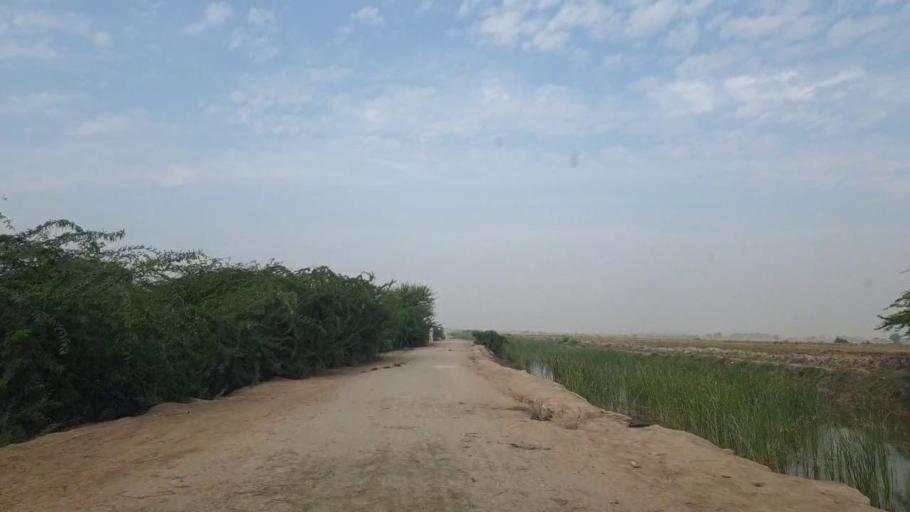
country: PK
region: Sindh
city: Tando Bago
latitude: 24.8638
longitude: 68.9938
